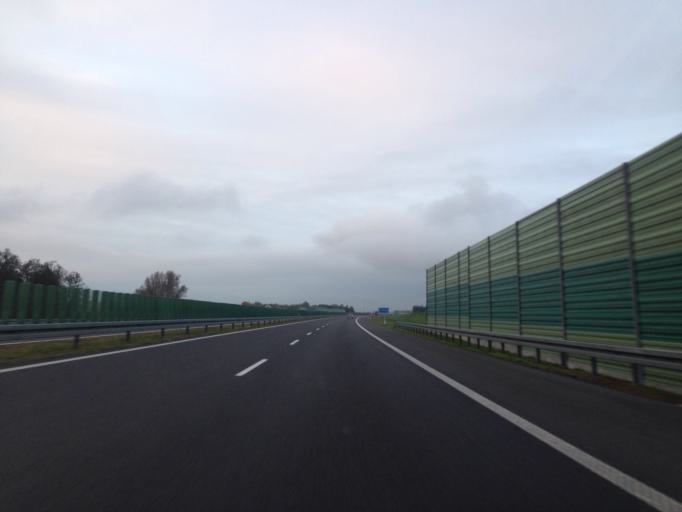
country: PL
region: Kujawsko-Pomorskie
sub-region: Powiat swiecki
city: Warlubie
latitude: 53.6158
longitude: 18.6325
